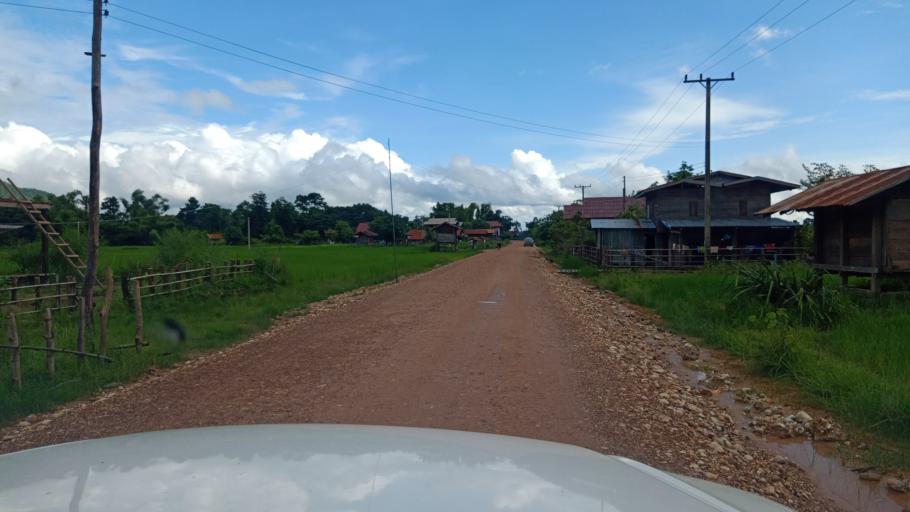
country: LA
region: Attapu
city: Attapu
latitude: 14.7362
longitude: 106.5516
